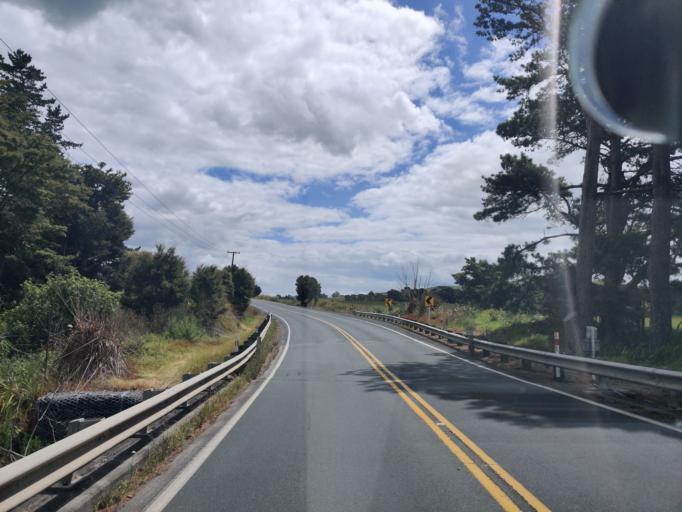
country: NZ
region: Northland
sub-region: Far North District
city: Paihia
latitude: -35.2814
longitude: 174.0389
